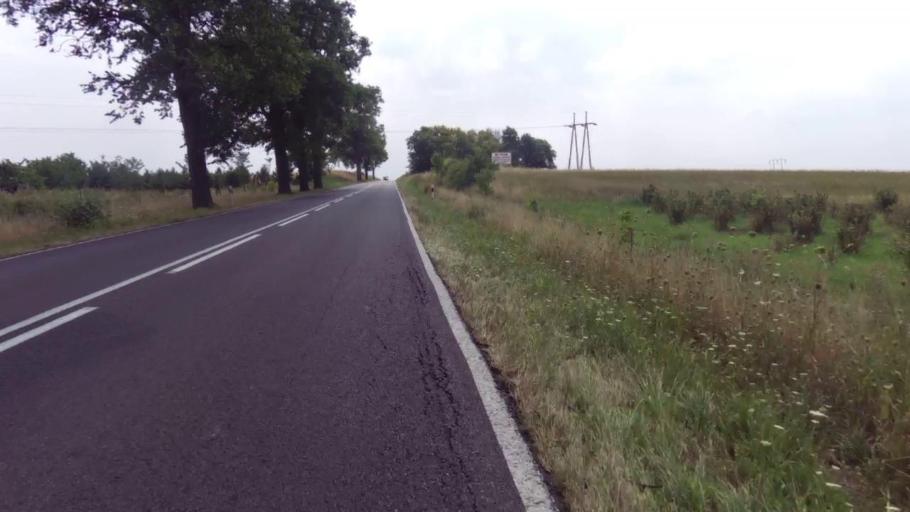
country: PL
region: West Pomeranian Voivodeship
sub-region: Powiat choszczenski
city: Choszczno
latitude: 53.1850
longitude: 15.3996
